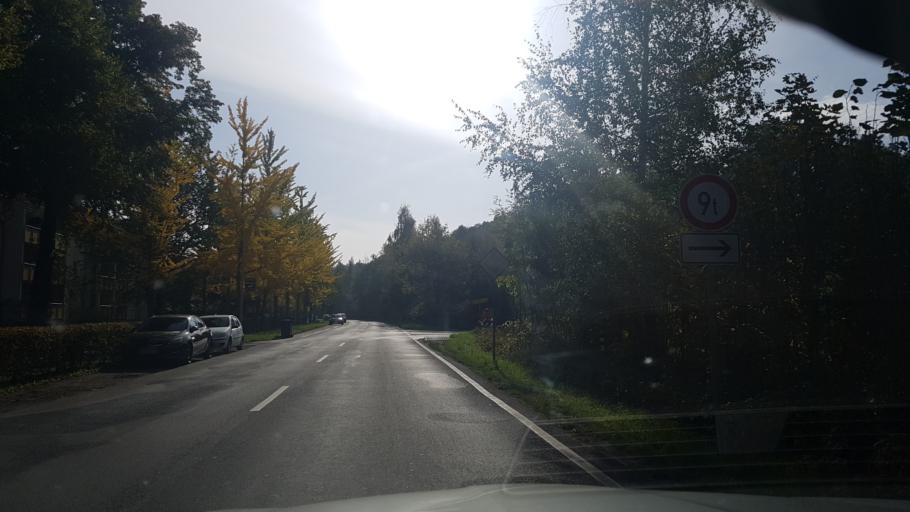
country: DE
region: Saxony
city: Dohma
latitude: 50.9335
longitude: 13.9481
